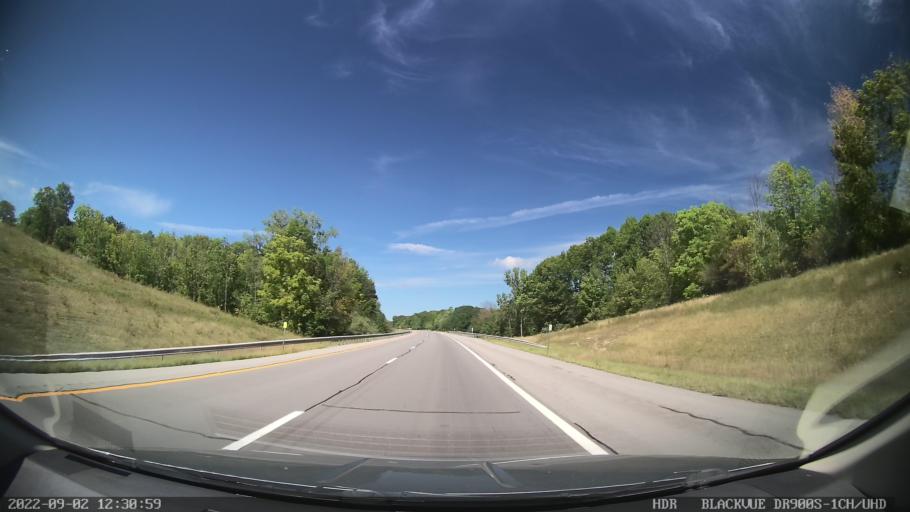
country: US
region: New York
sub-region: Livingston County
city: Dansville
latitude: 42.6020
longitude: -77.7528
